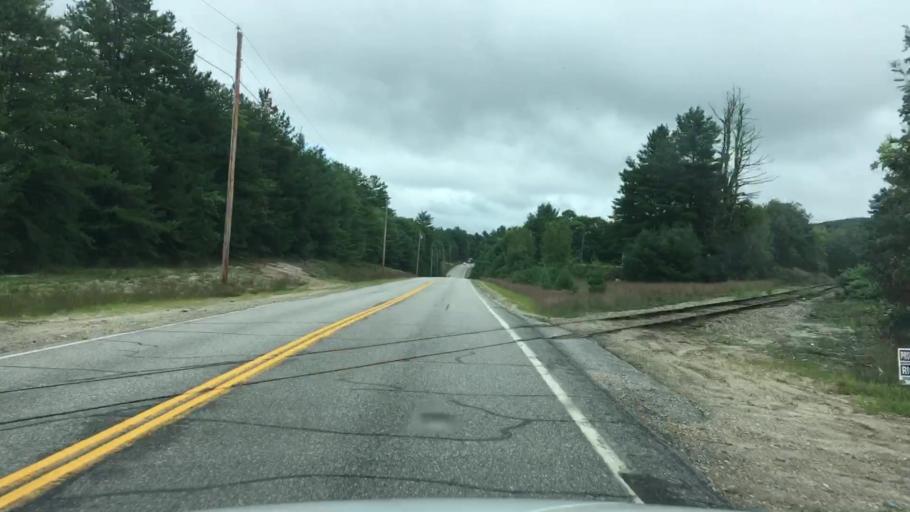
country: US
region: Maine
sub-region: Oxford County
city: Hiram
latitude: 43.8994
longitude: -70.8347
